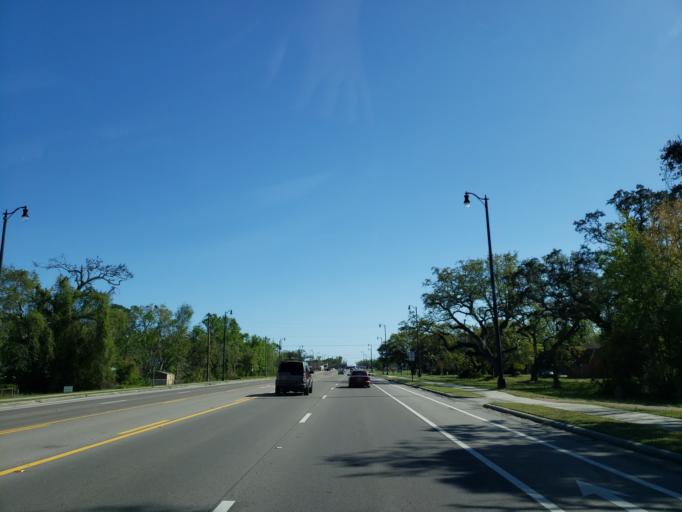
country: US
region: Mississippi
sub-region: Harrison County
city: West Gulfport
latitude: 30.3955
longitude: -89.0268
